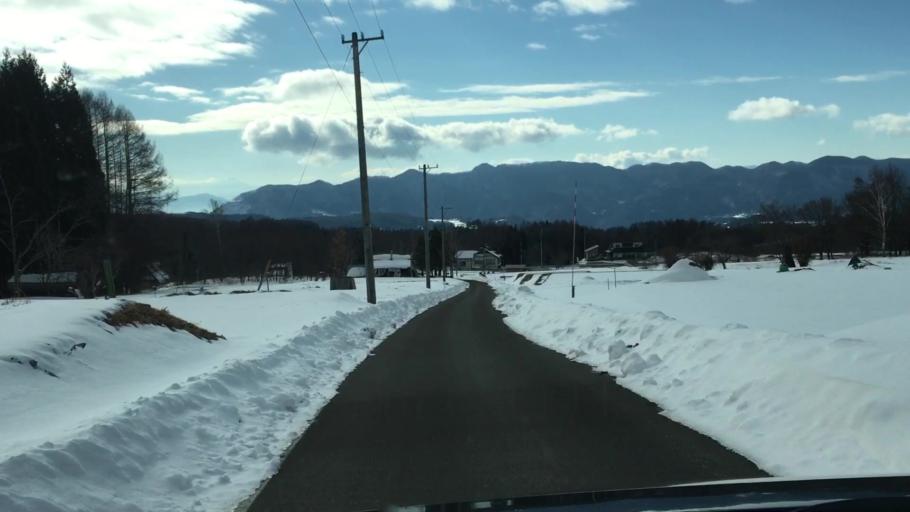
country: JP
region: Nagano
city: Nagano-shi
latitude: 36.7291
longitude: 138.0854
